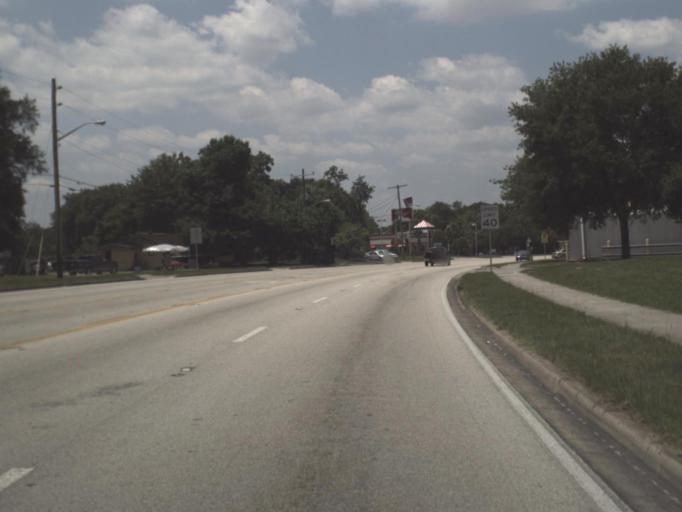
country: US
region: Florida
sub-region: Duval County
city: Jacksonville
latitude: 30.3796
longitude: -81.6966
